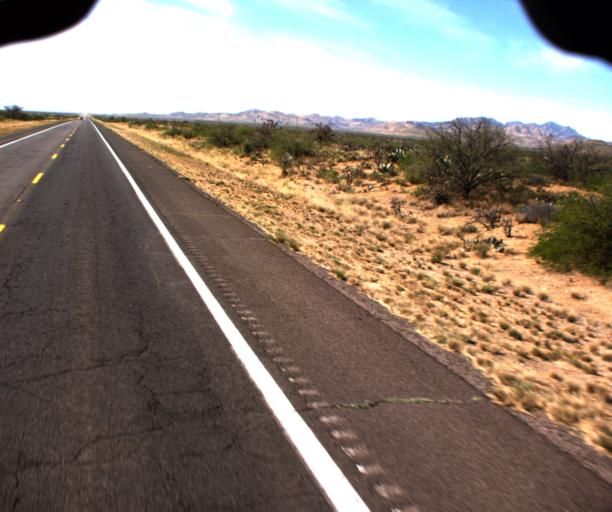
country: US
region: Arizona
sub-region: Graham County
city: Swift Trail Junction
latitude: 32.6116
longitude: -109.6876
